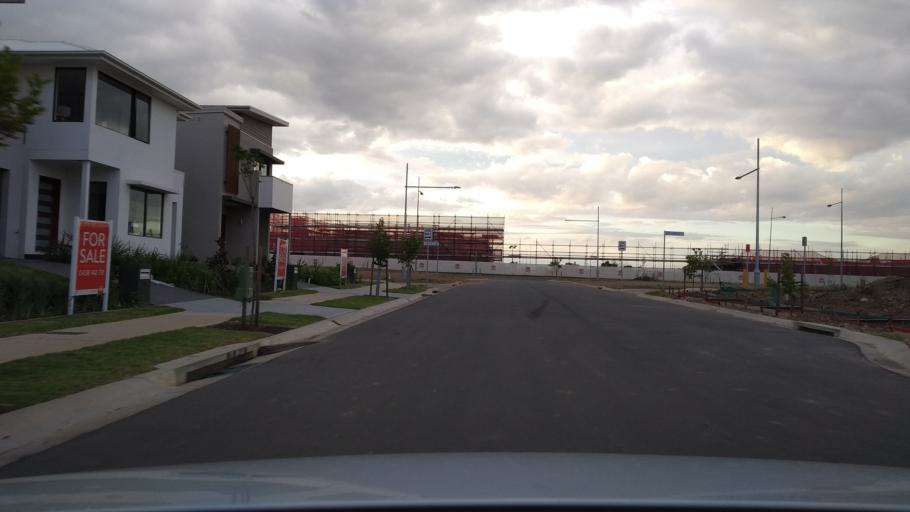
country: AU
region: New South Wales
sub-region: Camden
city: Narellan
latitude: -33.9999
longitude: 150.7365
